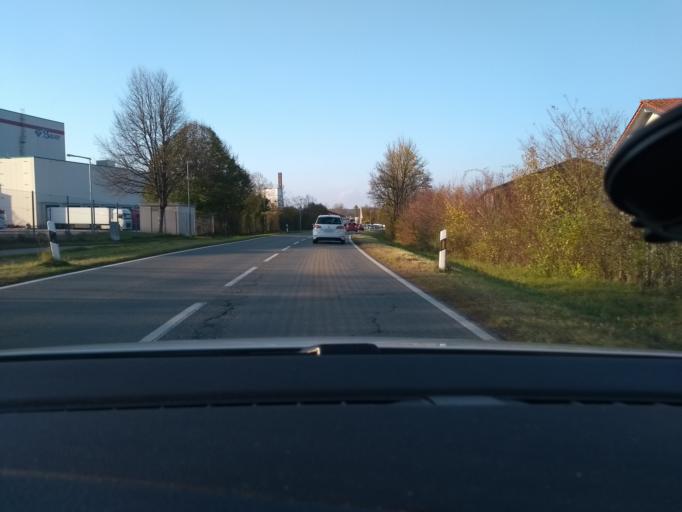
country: DE
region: Bavaria
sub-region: Upper Bavaria
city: Wasserburg am Inn
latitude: 48.0470
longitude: 12.2231
